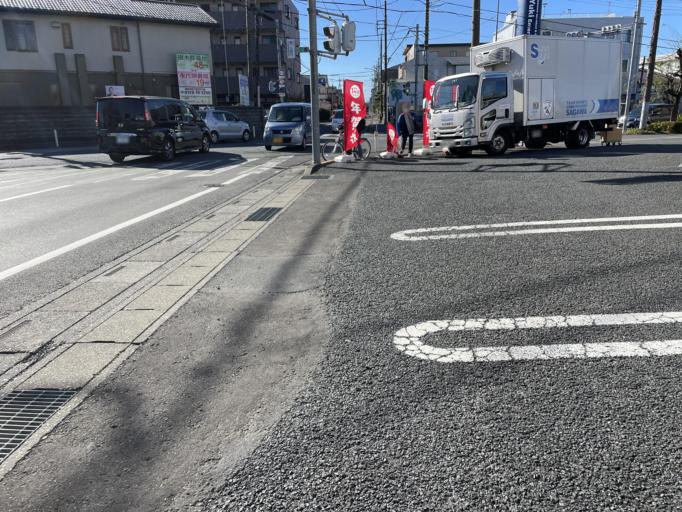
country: JP
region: Saitama
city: Sakado
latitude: 35.9301
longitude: 139.4157
